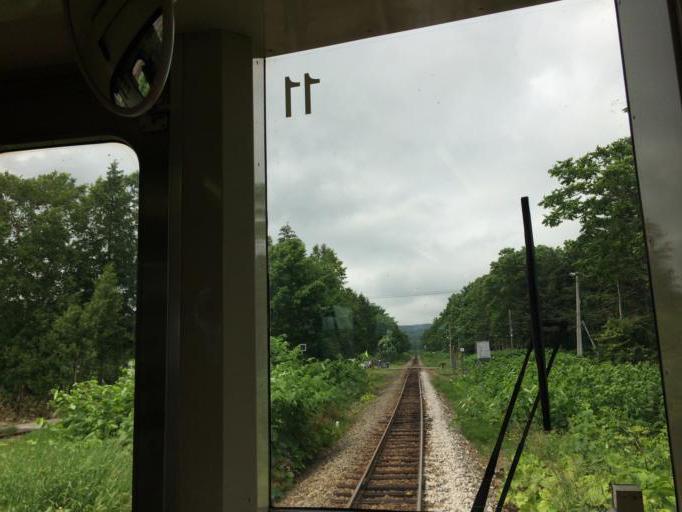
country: JP
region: Hokkaido
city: Niseko Town
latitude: 42.9087
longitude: 140.7447
